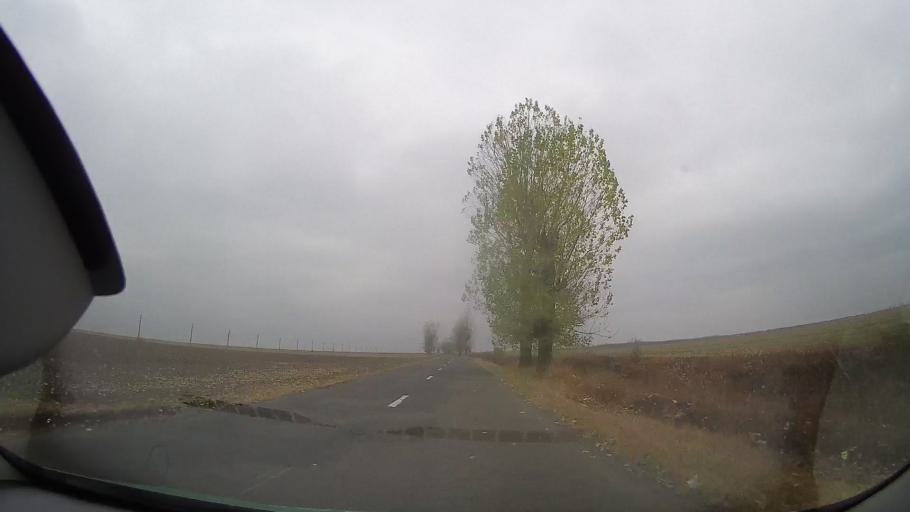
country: RO
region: Ialomita
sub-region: Comuna Grindu
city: Grindu
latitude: 44.7959
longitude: 26.8892
